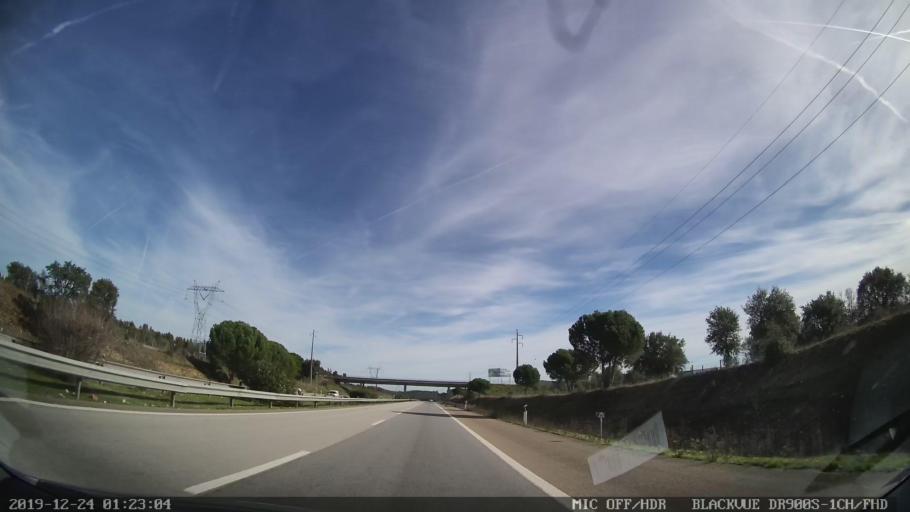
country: PT
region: Santarem
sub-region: Abrantes
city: Abrantes
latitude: 39.4949
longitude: -8.1939
